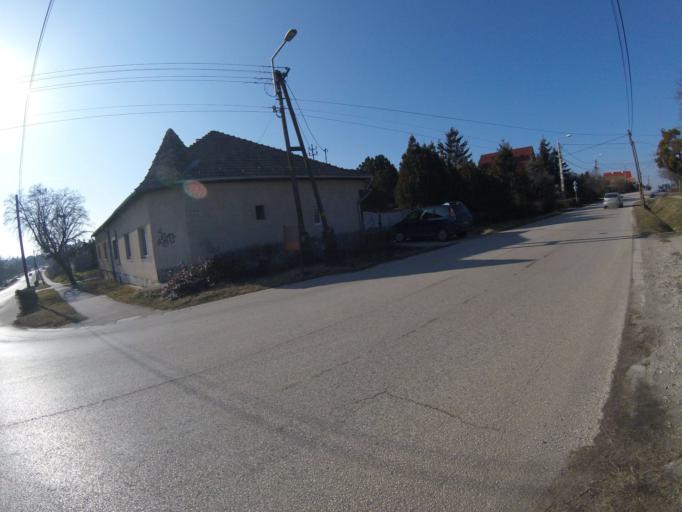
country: HU
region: Komarom-Esztergom
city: Oroszlany
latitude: 47.4852
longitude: 18.3261
